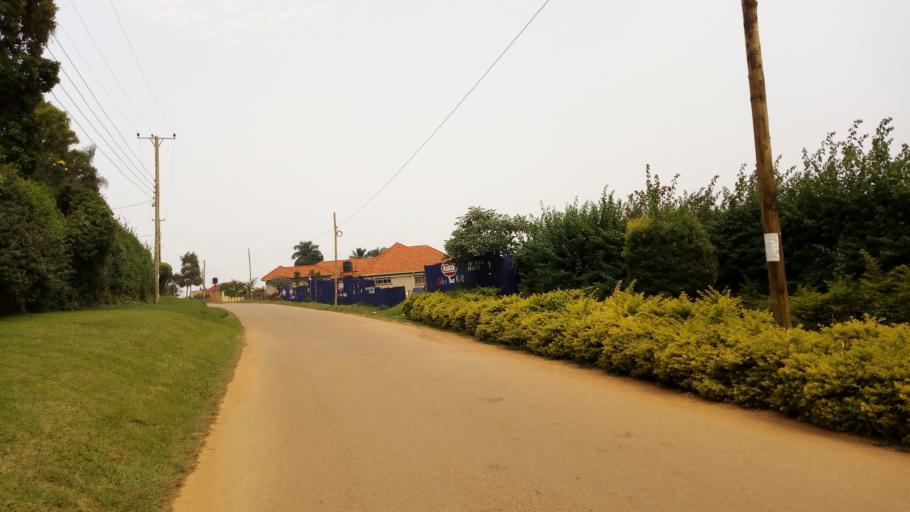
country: UG
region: Central Region
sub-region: Wakiso District
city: Kireka
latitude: 0.3140
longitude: 32.6399
